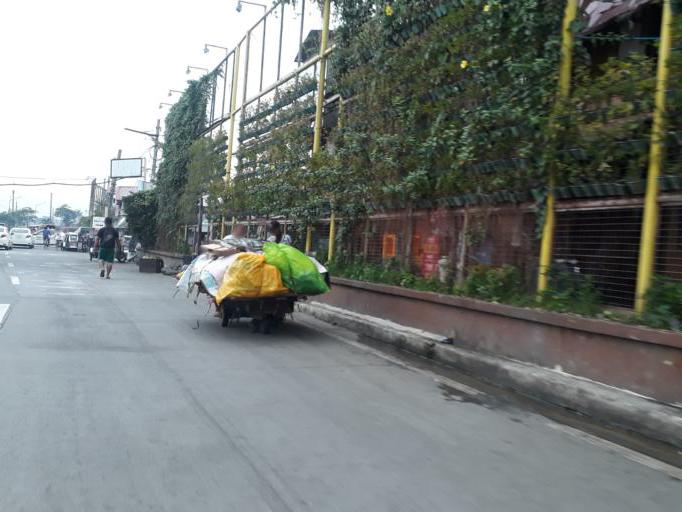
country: PH
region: Metro Manila
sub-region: Caloocan City
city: Niugan
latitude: 14.6543
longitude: 120.9551
